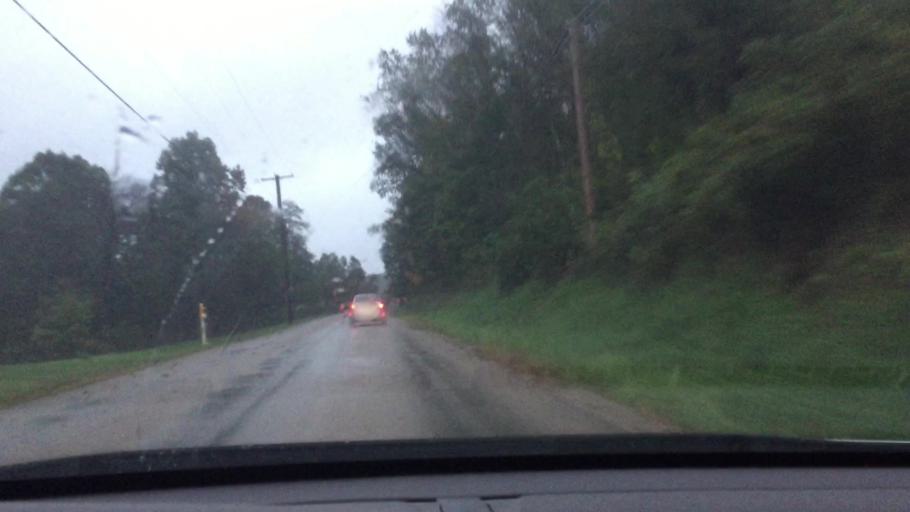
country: US
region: Pennsylvania
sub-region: Washington County
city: Bentleyville
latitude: 40.1299
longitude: -79.9693
